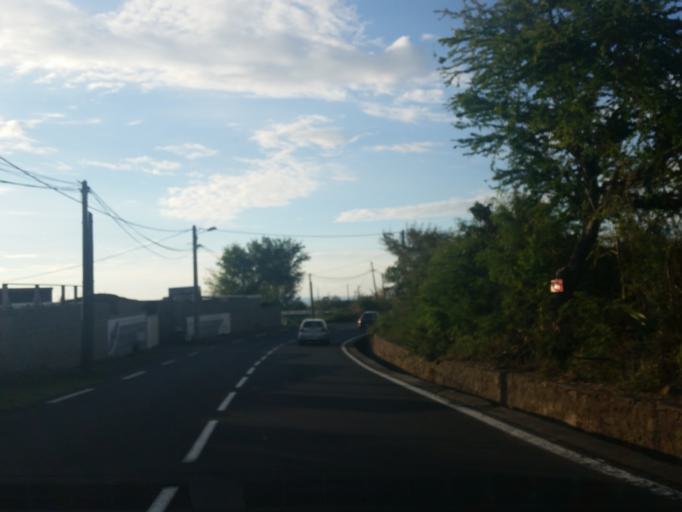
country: RE
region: Reunion
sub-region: Reunion
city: Saint-Leu
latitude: -21.1401
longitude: 55.2828
